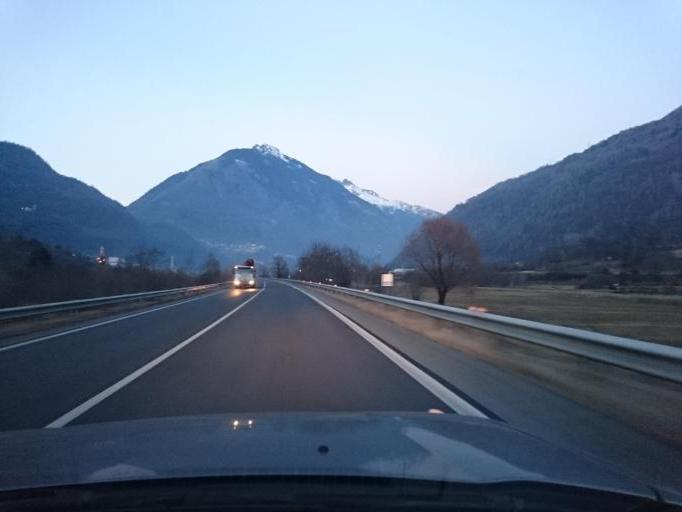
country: IT
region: Lombardy
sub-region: Provincia di Sondrio
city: Grosotto
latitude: 46.2695
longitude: 10.2590
